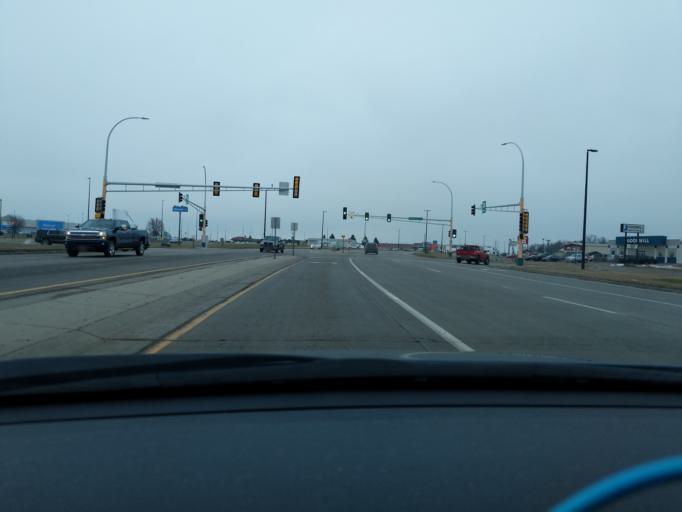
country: US
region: Minnesota
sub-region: Lyon County
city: Marshall
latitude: 44.4346
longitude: -95.7718
